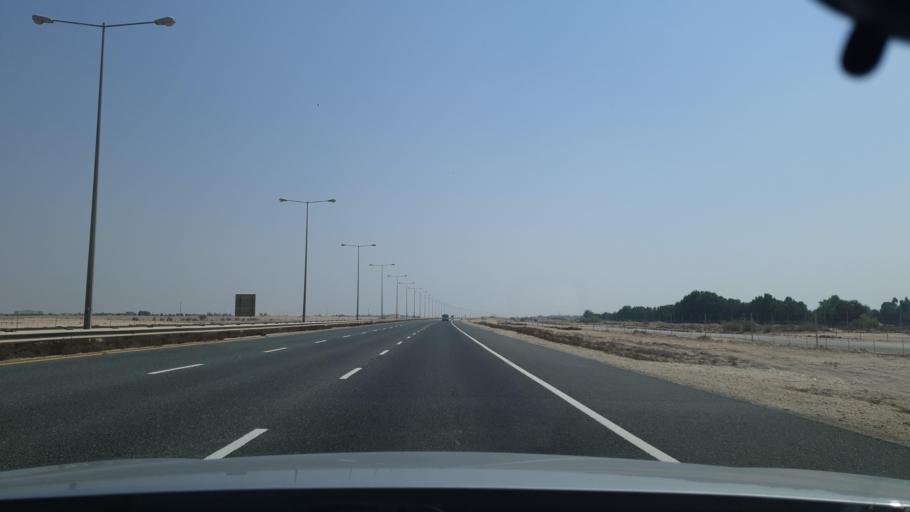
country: QA
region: Al Khawr
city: Al Khawr
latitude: 25.7807
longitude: 51.4029
